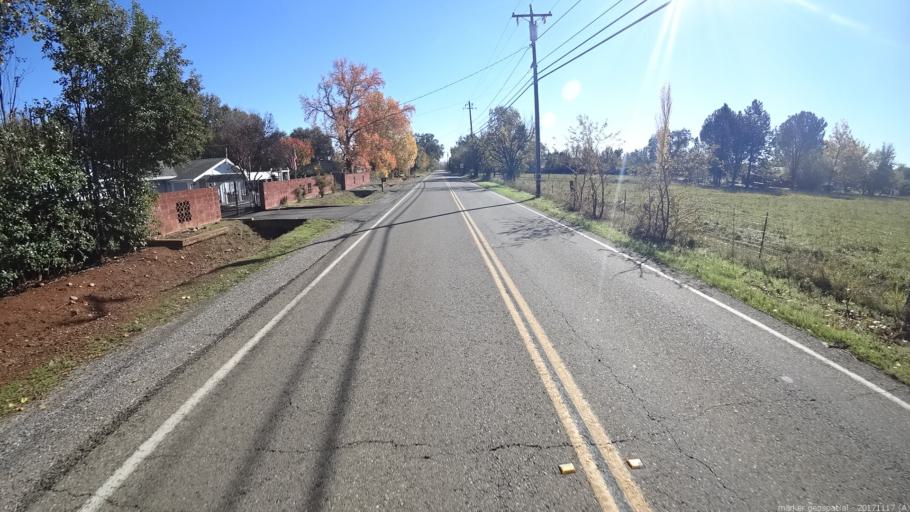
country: US
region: California
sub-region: Shasta County
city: Cottonwood
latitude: 40.4276
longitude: -122.2270
